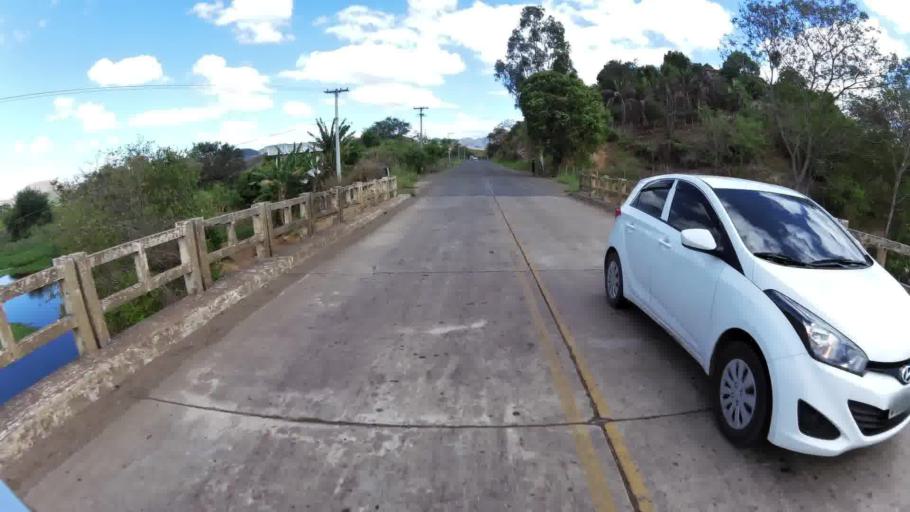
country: BR
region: Rio de Janeiro
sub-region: Itaperuna
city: Itaperuna
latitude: -21.2737
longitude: -41.7839
